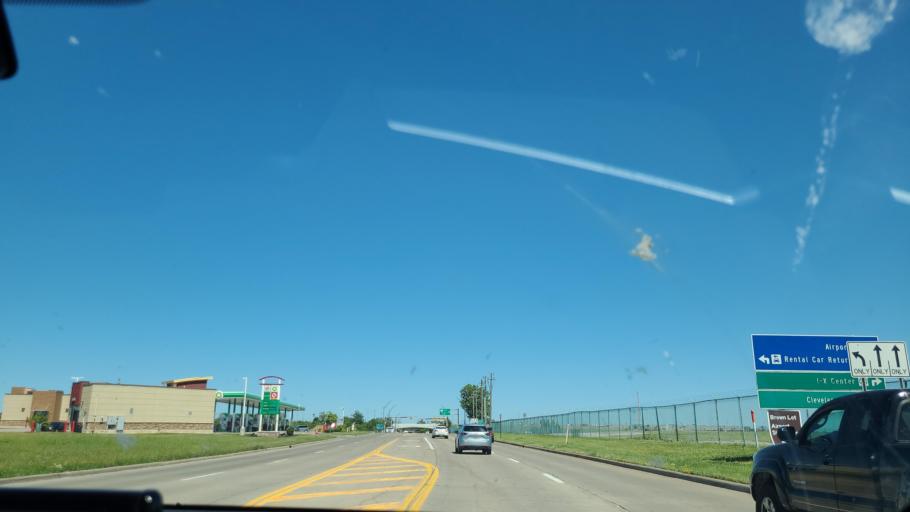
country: US
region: Ohio
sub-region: Cuyahoga County
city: Brook Park
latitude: 41.4187
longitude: -81.8342
